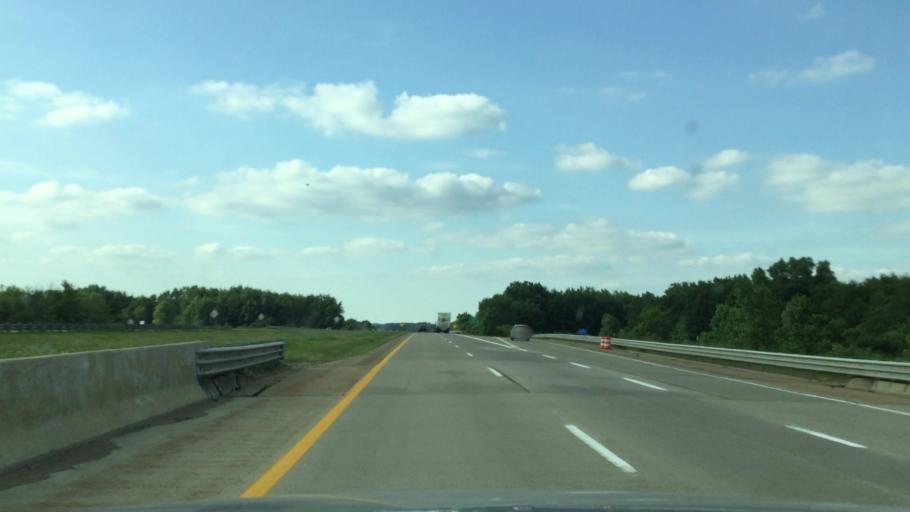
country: US
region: Michigan
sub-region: Branch County
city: Union City
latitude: 42.1004
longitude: -84.9965
